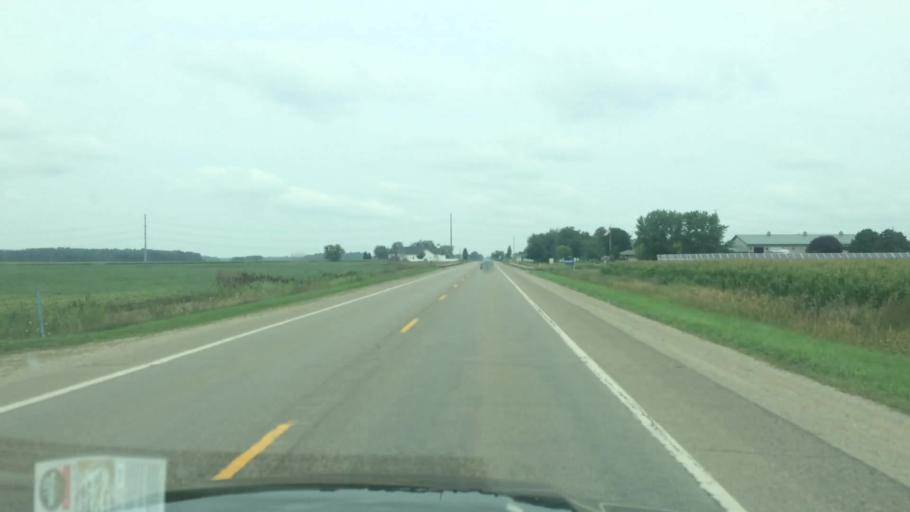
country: US
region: Michigan
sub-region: Huron County
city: Bad Axe
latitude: 43.8343
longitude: -83.0013
